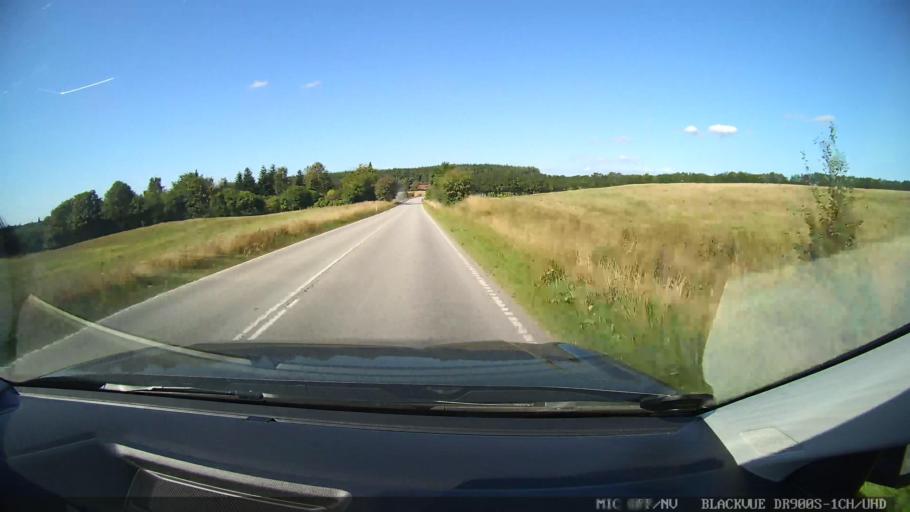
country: DK
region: North Denmark
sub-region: Mariagerfjord Kommune
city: Mariager
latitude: 56.6257
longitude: 9.9804
